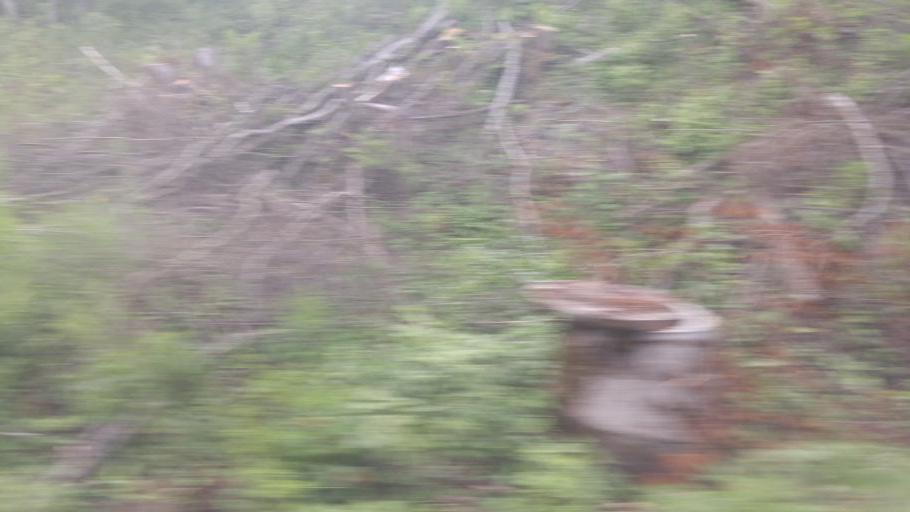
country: NO
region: Sor-Trondelag
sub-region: Melhus
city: Lundamo
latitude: 63.1602
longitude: 10.2882
